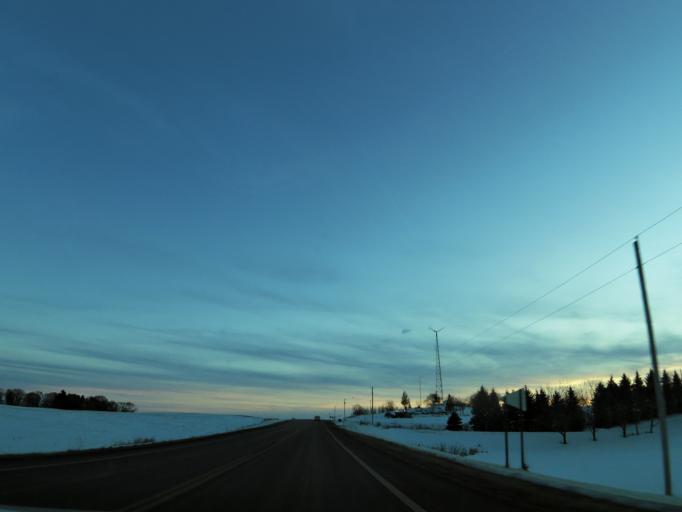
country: US
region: Minnesota
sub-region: Carver County
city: Chaska
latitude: 44.7519
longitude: -93.5615
